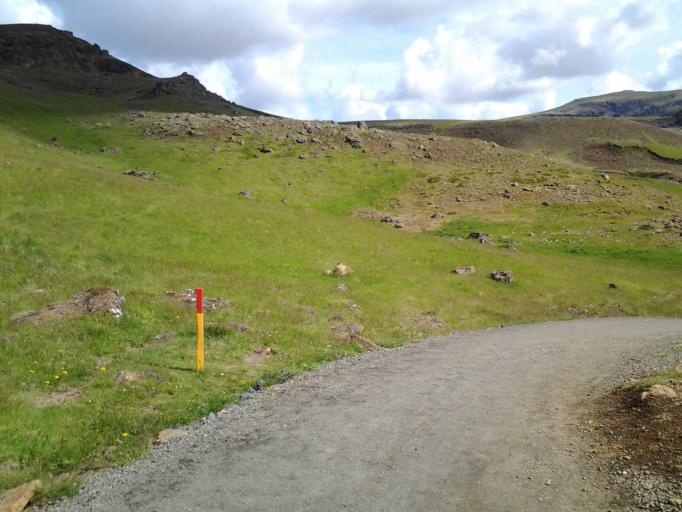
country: IS
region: South
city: Hveragerdi
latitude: 64.0282
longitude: -21.2124
